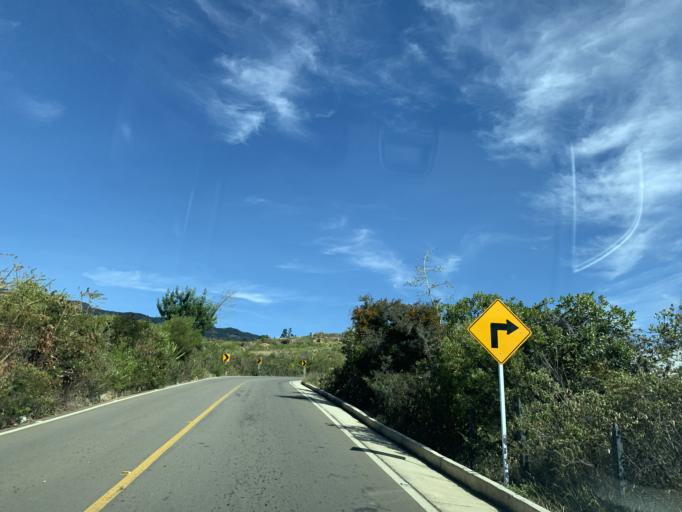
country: CO
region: Boyaca
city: Santa Sofia
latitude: 5.6909
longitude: -73.5888
